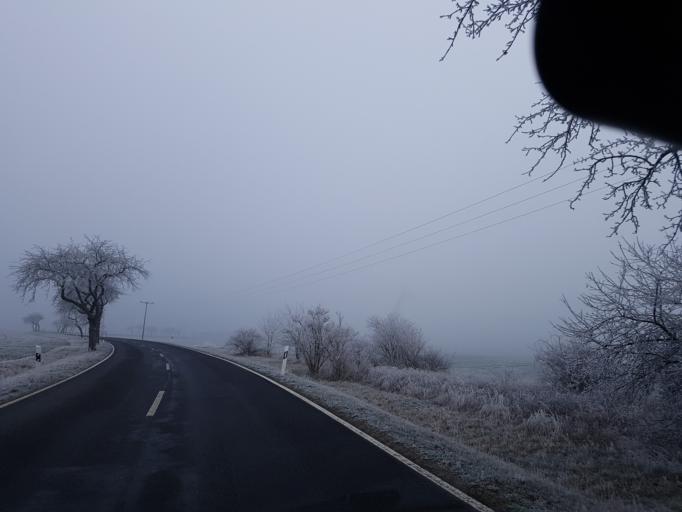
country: DE
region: Brandenburg
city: Muhlberg
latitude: 51.4279
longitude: 13.2420
